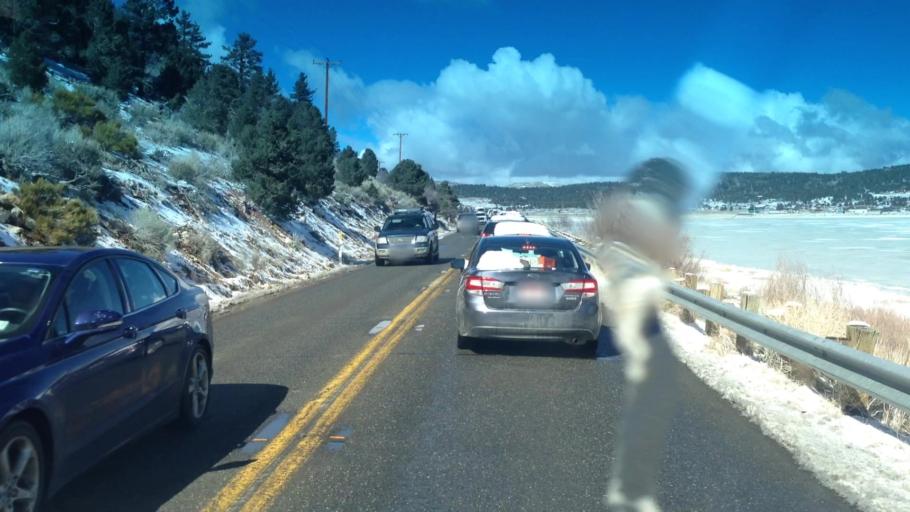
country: US
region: California
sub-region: San Bernardino County
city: Big Bear City
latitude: 34.2788
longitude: -116.8143
